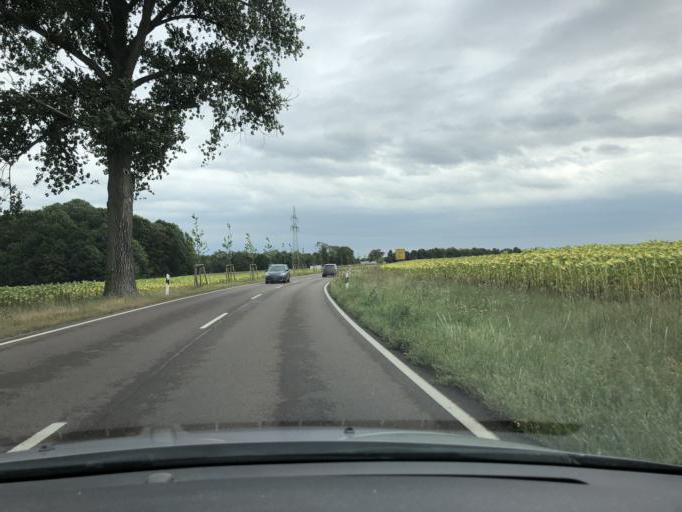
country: DE
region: Saxony-Anhalt
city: Koethen
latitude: 51.7583
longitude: 11.9397
